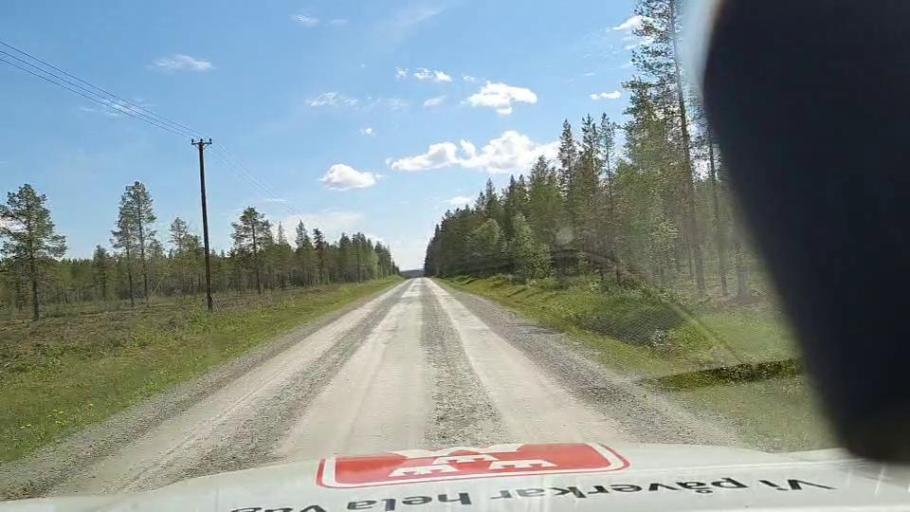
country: SE
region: Jaemtland
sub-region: Stroemsunds Kommun
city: Stroemsund
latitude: 64.4771
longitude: 15.5931
